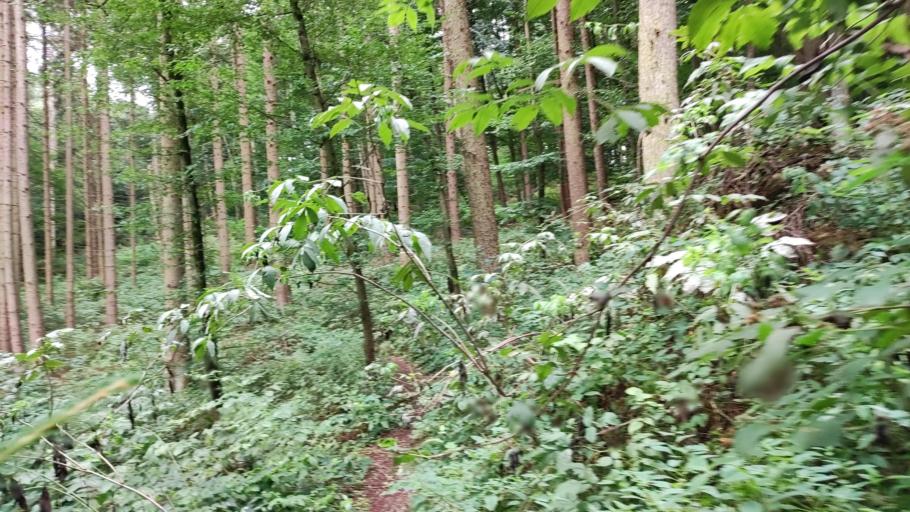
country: DE
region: Bavaria
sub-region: Swabia
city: Jettingen-Scheppach
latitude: 48.3859
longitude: 10.3999
